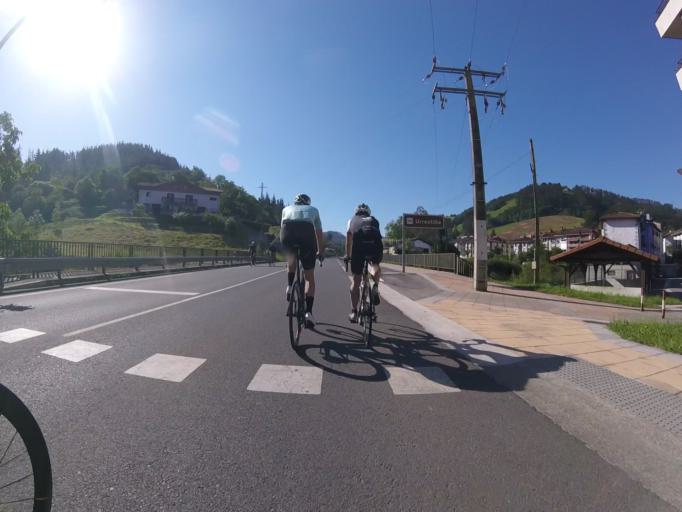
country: ES
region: Basque Country
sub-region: Provincia de Guipuzcoa
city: Azpeitia
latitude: 43.1586
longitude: -2.2441
